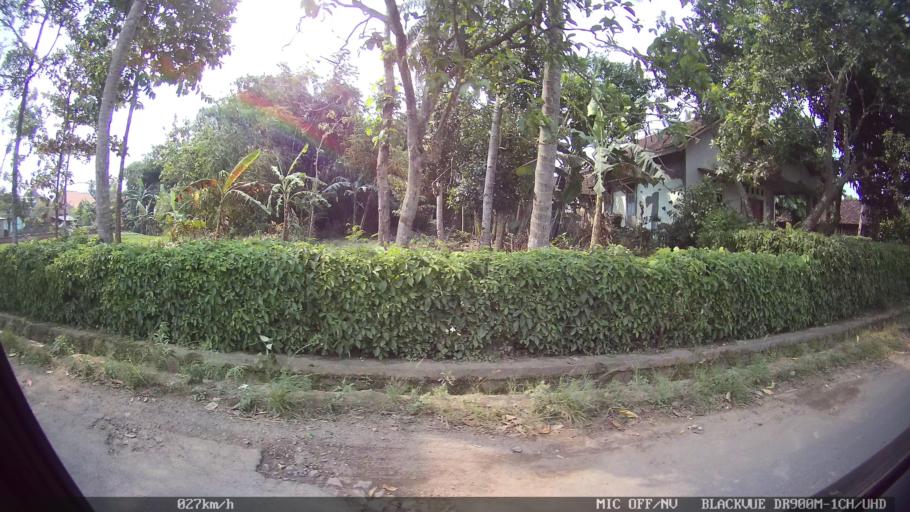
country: ID
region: Lampung
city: Gadingrejo
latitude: -5.3514
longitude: 105.0210
